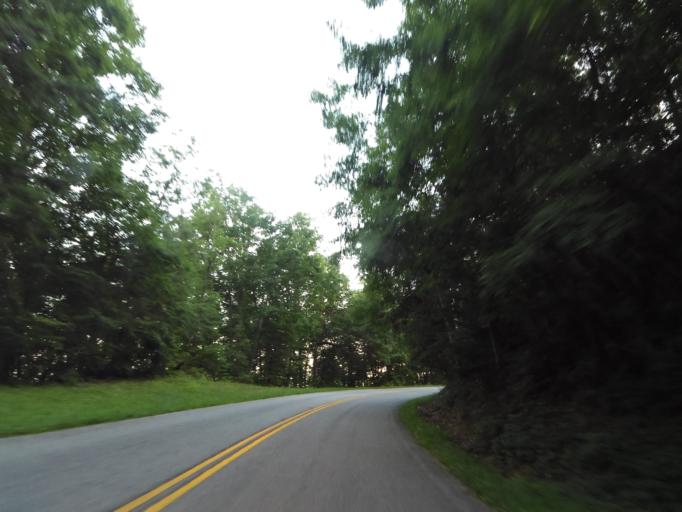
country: US
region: Tennessee
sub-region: Blount County
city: Maryville
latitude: 35.6275
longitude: -83.9498
